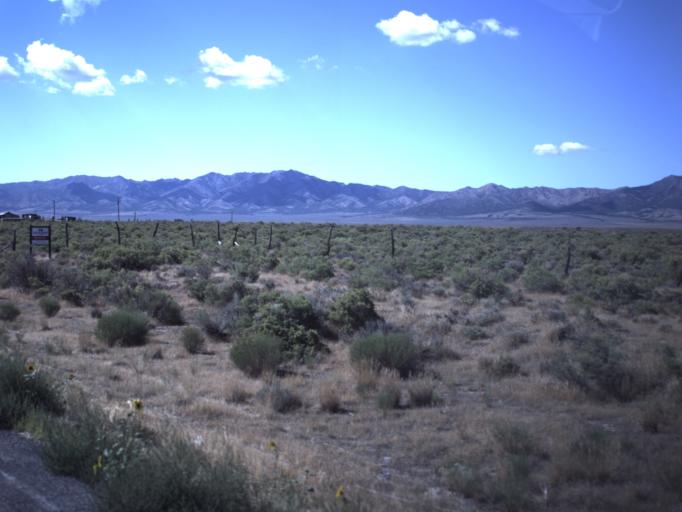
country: US
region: Utah
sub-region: Tooele County
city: Tooele
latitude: 40.1221
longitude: -112.4308
